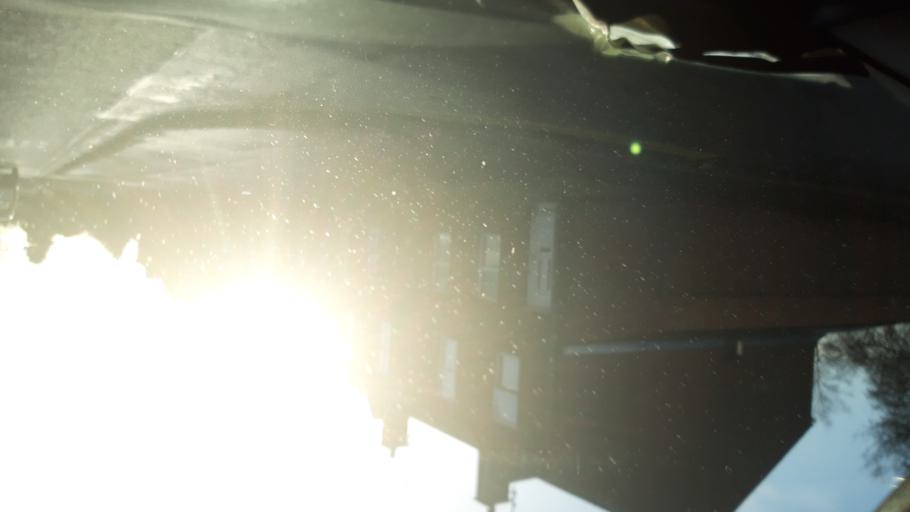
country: GB
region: Northern Ireland
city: Maghera
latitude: 54.8438
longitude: -6.6749
